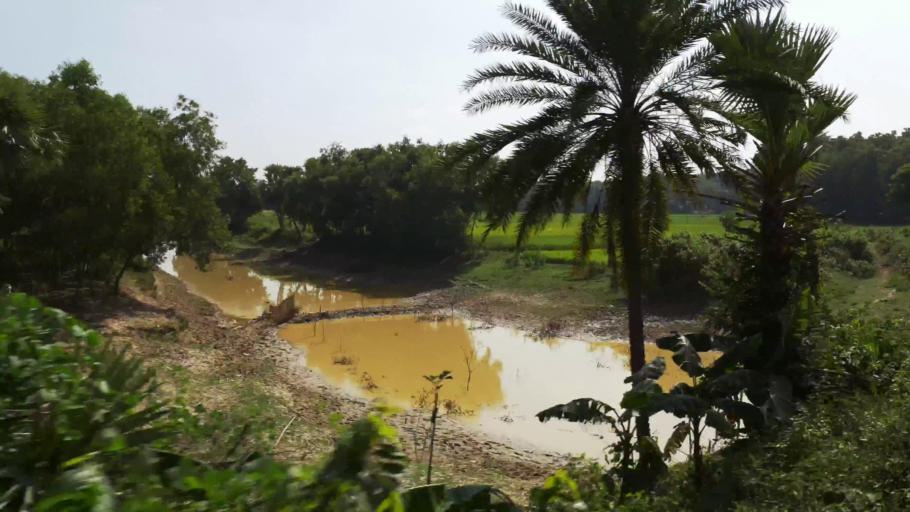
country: BD
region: Dhaka
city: Tungi
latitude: 24.1465
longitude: 90.4638
